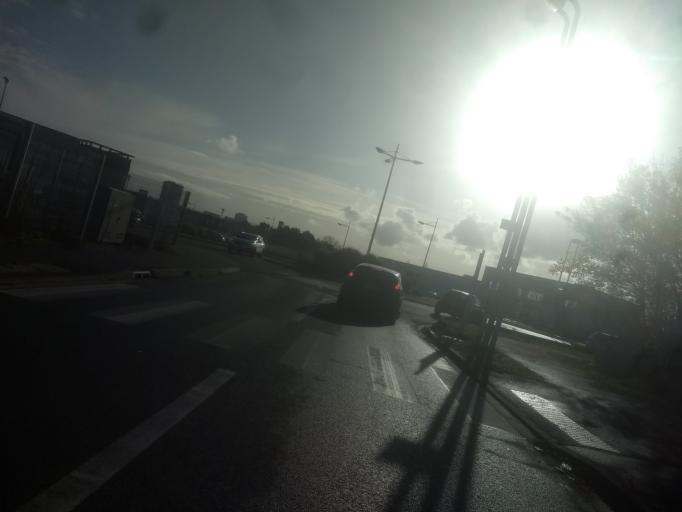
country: FR
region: Nord-Pas-de-Calais
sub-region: Departement du Pas-de-Calais
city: Anzin-Saint-Aubin
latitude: 50.3039
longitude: 2.7357
